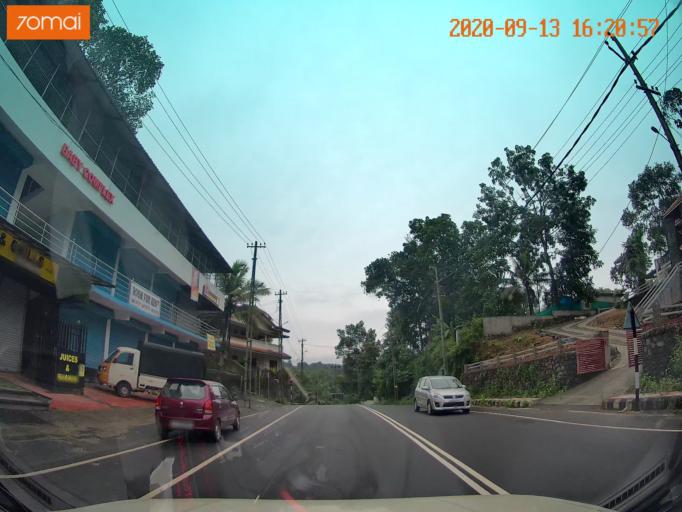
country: IN
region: Kerala
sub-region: Kottayam
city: Lalam
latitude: 9.7056
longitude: 76.6639
